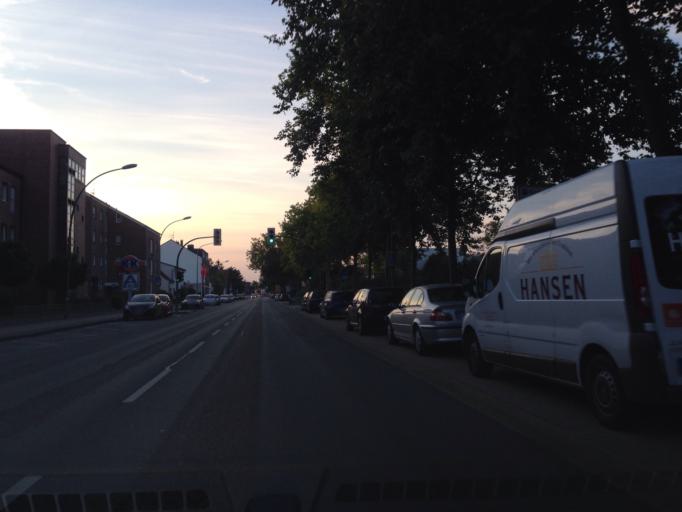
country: DE
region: North Rhine-Westphalia
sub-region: Regierungsbezirk Munster
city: Muenster
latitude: 51.8993
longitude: 7.6407
